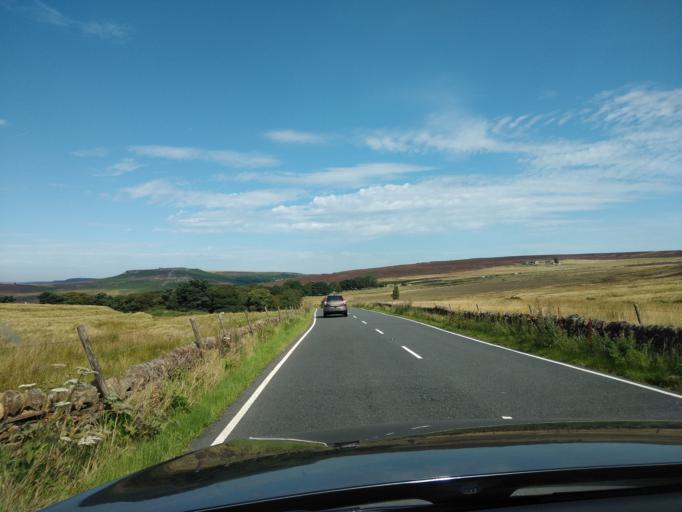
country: GB
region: England
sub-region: Derbyshire
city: Hathersage
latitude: 53.3139
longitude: -1.5990
